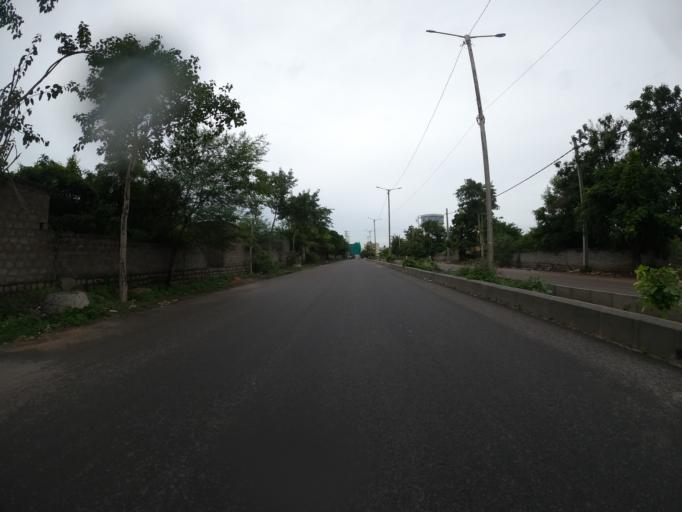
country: IN
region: Telangana
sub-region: Rangareddi
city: Kukatpalli
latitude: 17.4601
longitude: 78.3949
